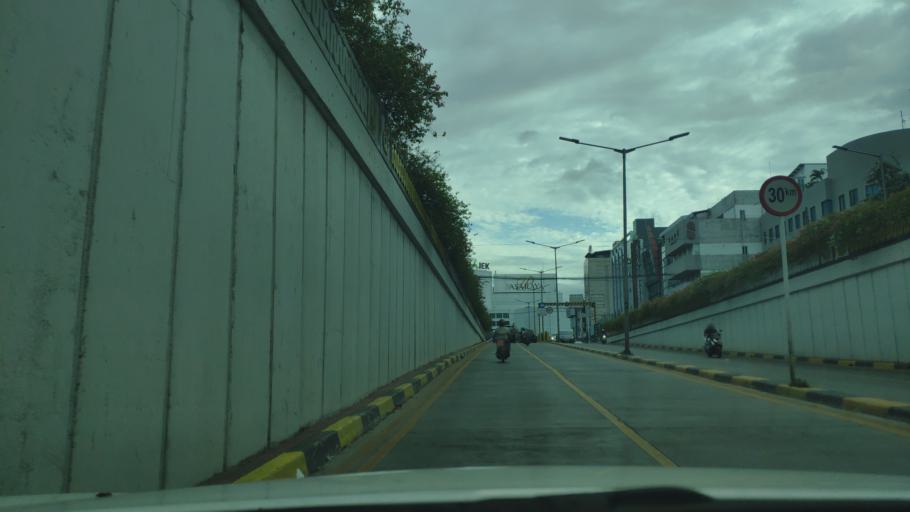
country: ID
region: Jakarta Raya
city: Jakarta
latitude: -6.2406
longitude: 106.8025
